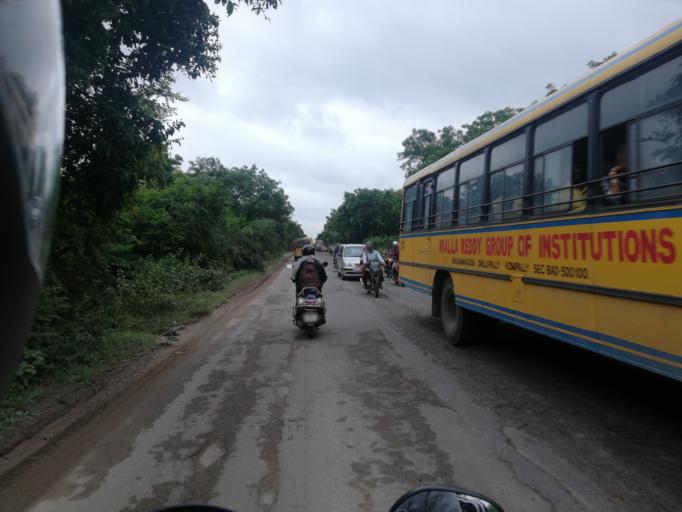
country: IN
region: Telangana
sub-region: Rangareddi
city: Quthbullapur
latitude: 17.5608
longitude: 78.4121
